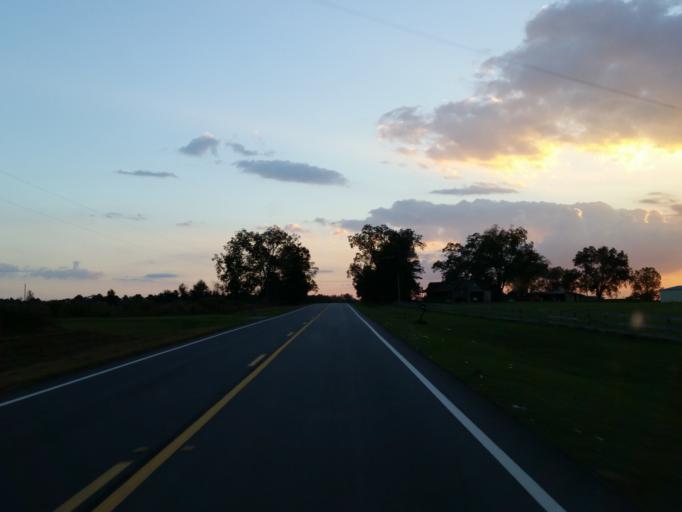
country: US
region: Georgia
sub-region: Pulaski County
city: Hawkinsville
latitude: 32.1863
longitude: -83.5866
